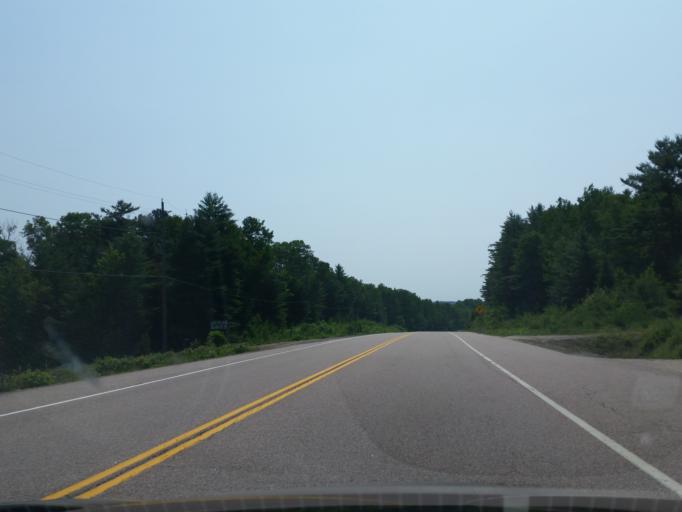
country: CA
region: Ontario
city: Deep River
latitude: 46.2112
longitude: -77.8911
